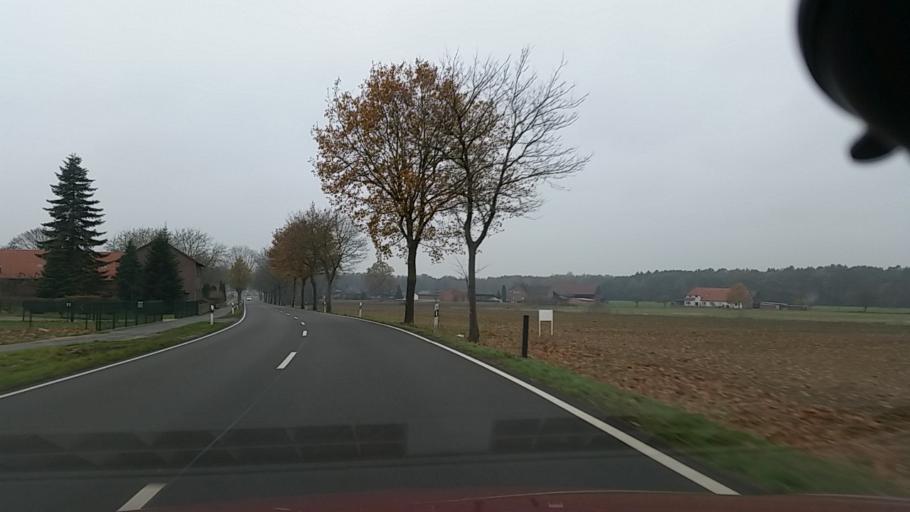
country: DE
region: Lower Saxony
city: Wittingen
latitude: 52.7284
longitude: 10.6819
